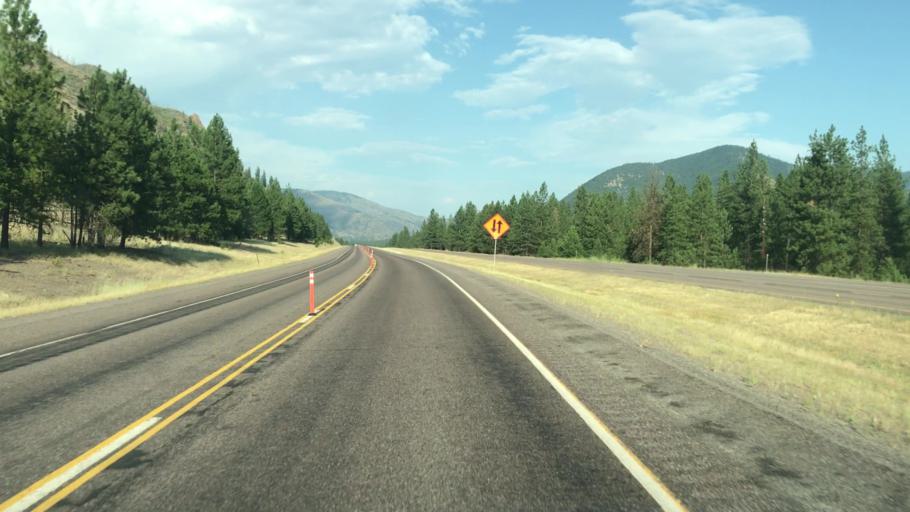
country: US
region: Montana
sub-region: Mineral County
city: Superior
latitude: 47.0117
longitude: -114.7190
